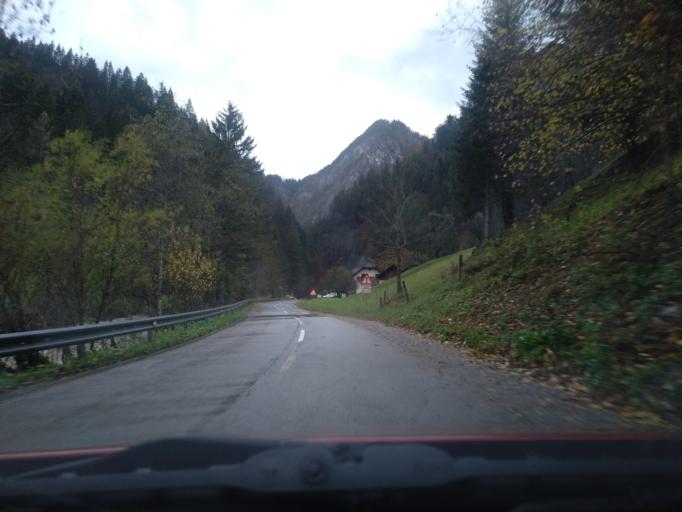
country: SI
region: Solcava
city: Solcava
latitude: 46.4207
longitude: 14.6706
